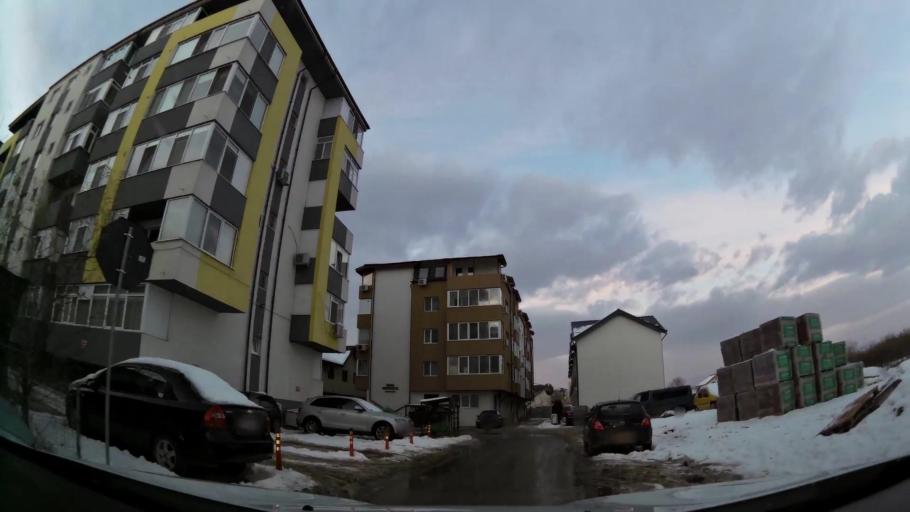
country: RO
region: Ilfov
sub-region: Comuna Popesti-Leordeni
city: Popesti-Leordeni
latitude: 44.3708
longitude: 26.1567
